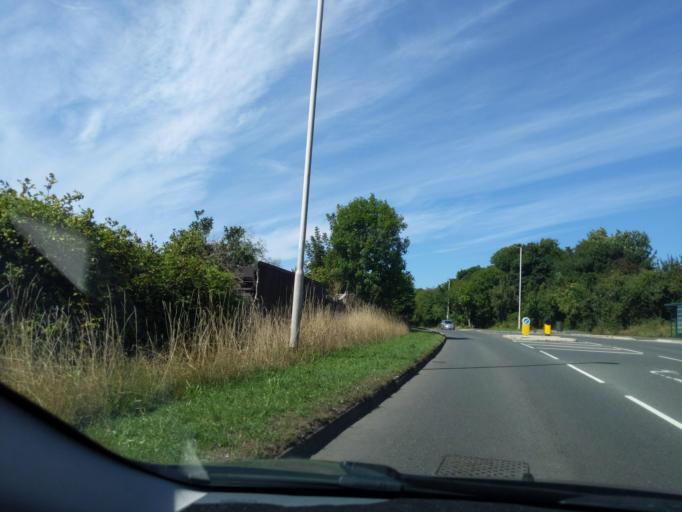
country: GB
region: England
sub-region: Devon
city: Plympton
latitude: 50.3873
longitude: -4.0317
